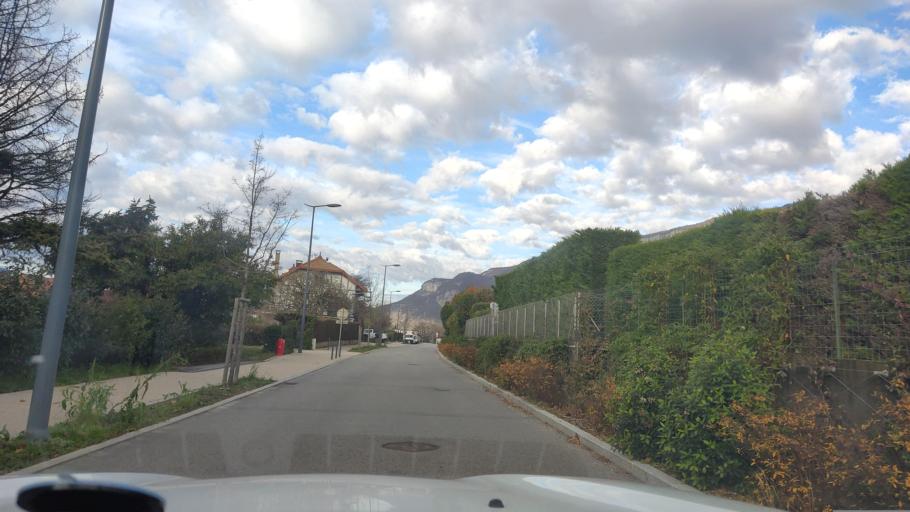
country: FR
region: Rhone-Alpes
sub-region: Departement de la Savoie
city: Brison-Saint-Innocent
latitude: 45.7257
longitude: 5.8880
